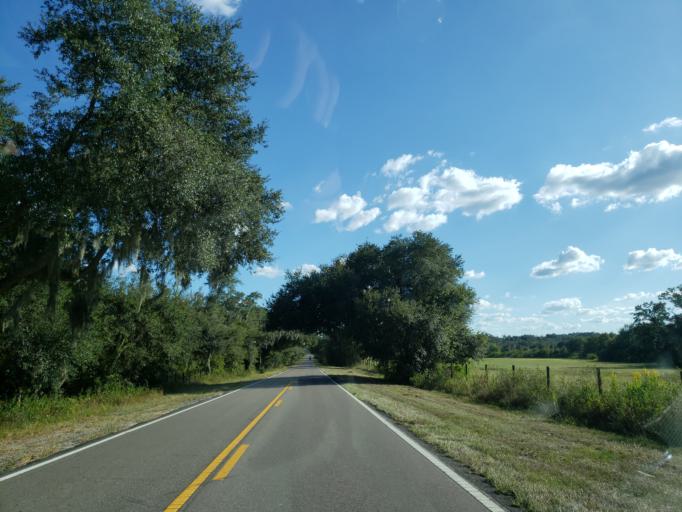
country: US
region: Florida
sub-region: Hillsborough County
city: Valrico
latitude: 27.9561
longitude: -82.2196
